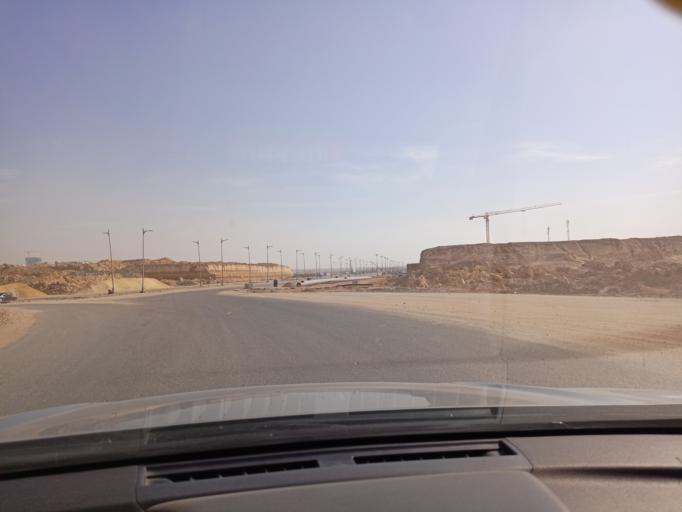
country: EG
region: Muhafazat al Qalyubiyah
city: Al Khankah
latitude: 30.0325
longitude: 31.6801
